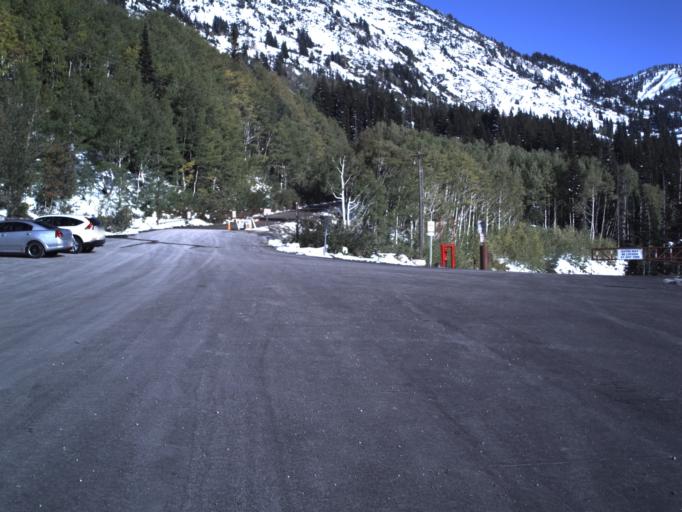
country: US
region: Utah
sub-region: Summit County
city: Snyderville
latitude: 40.5921
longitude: -111.6282
